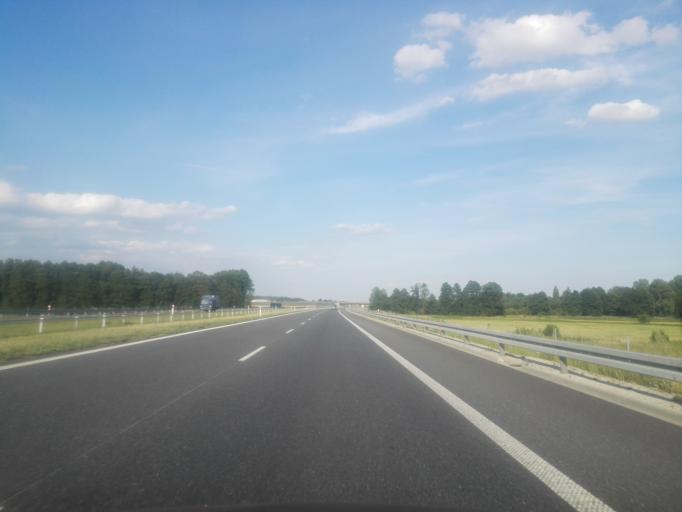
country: PL
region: Greater Poland Voivodeship
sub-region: Powiat kepinski
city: Kepno
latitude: 51.3159
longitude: 17.9672
